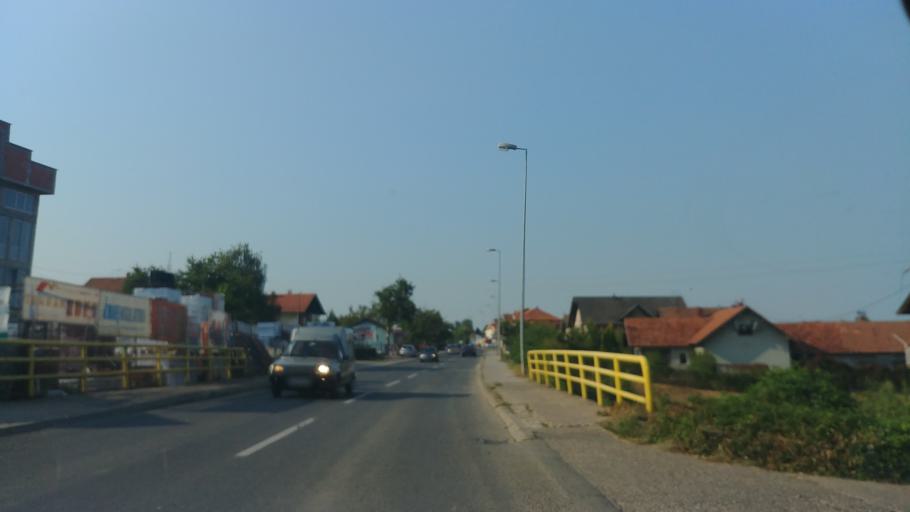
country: BA
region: Brcko
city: Brcko
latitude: 44.8534
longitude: 18.8144
